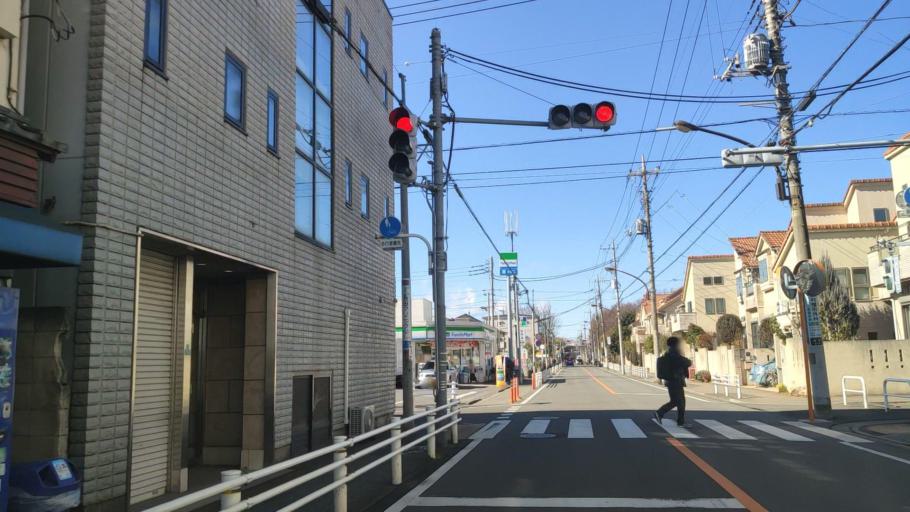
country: JP
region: Tokyo
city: Musashino
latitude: 35.7164
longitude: 139.5595
